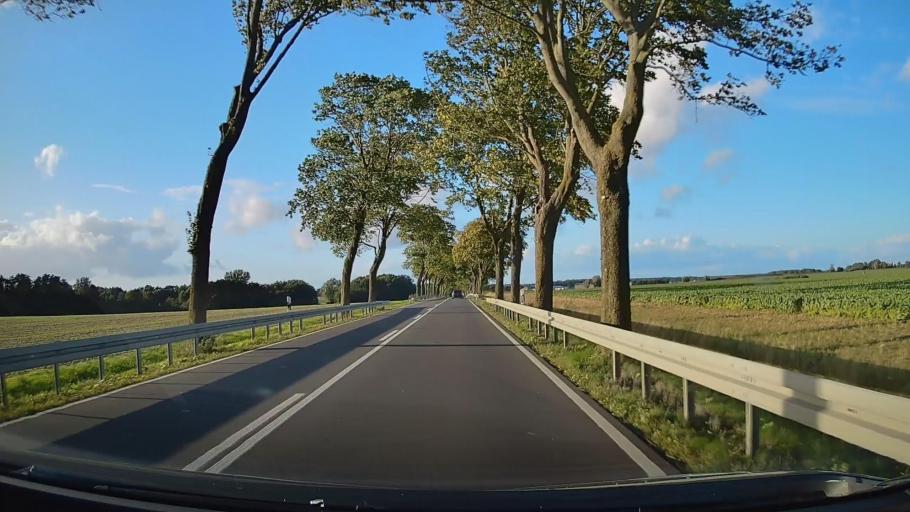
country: DE
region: Mecklenburg-Vorpommern
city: Steinhagen
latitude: 54.2166
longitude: 13.0044
